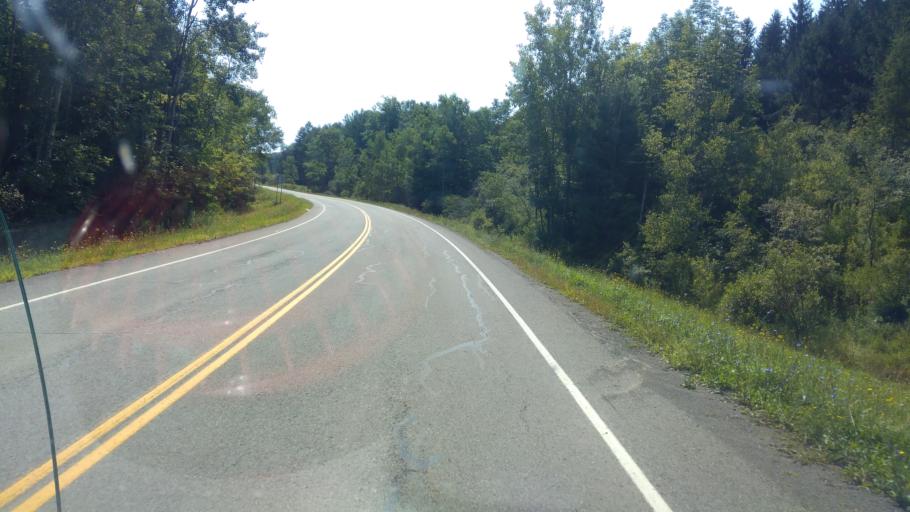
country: US
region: New York
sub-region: Allegany County
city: Belmont
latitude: 42.2986
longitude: -78.0120
